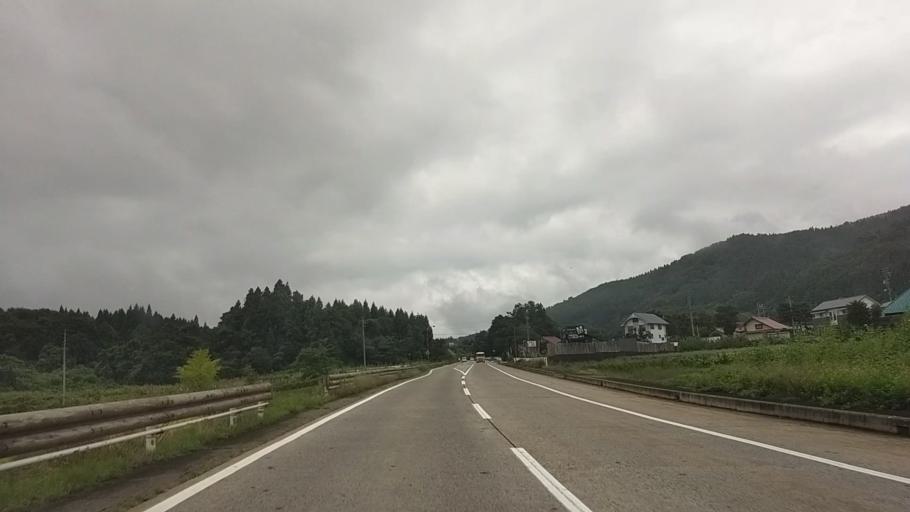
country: JP
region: Nagano
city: Iiyama
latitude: 36.8116
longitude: 138.3393
